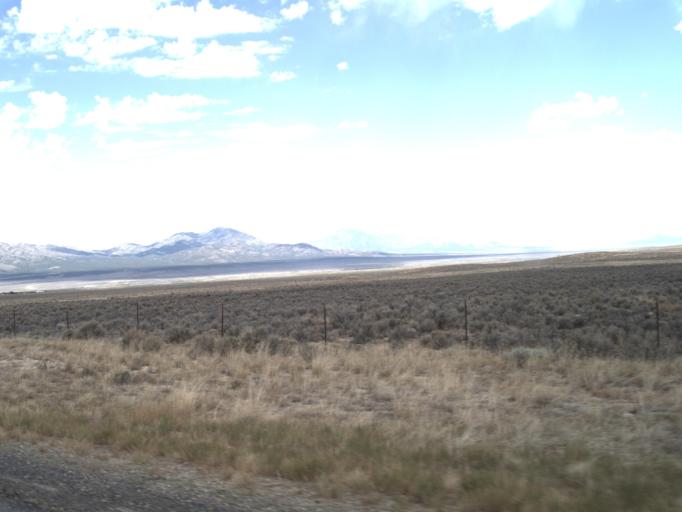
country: US
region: Utah
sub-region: Utah County
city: Eagle Mountain
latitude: 40.0786
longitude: -112.3975
